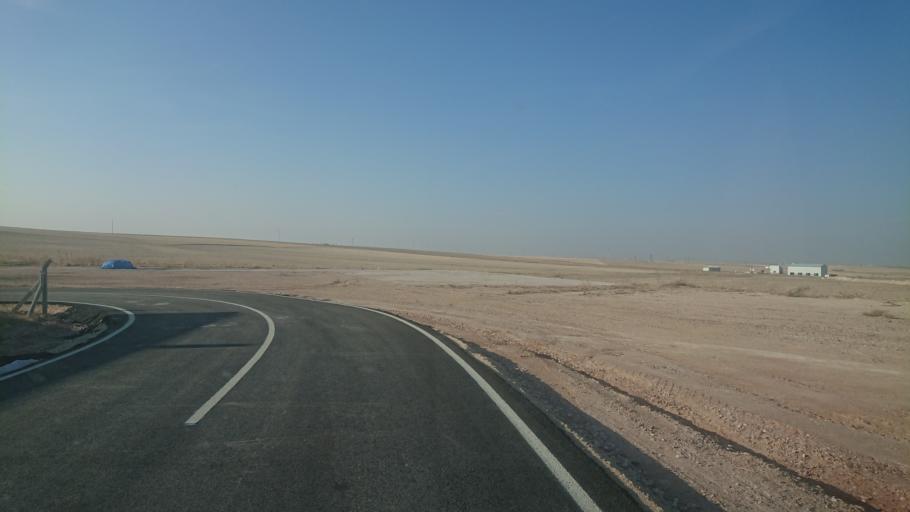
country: TR
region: Aksaray
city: Sultanhani
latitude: 38.0893
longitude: 33.6085
